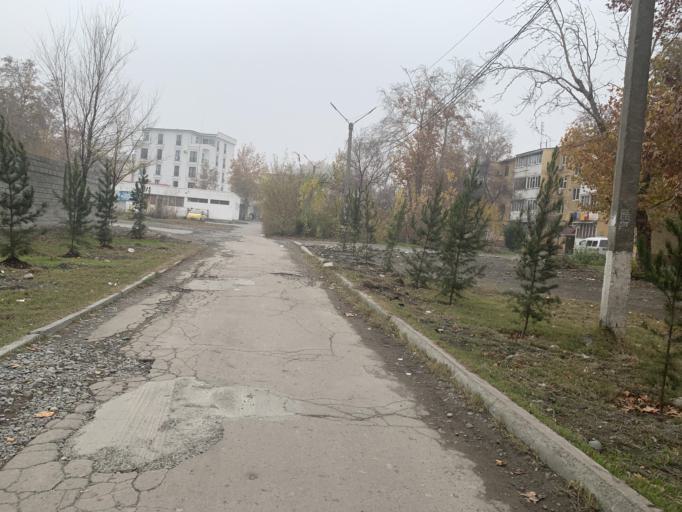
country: UZ
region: Fergana
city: Qo`qon
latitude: 40.5432
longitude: 70.9229
